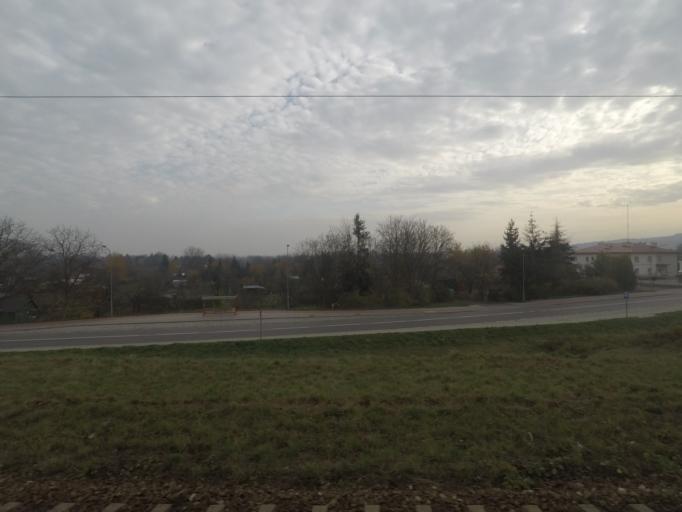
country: PL
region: Subcarpathian Voivodeship
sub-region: Przemysl
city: Przemysl
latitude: 49.7966
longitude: 22.7803
